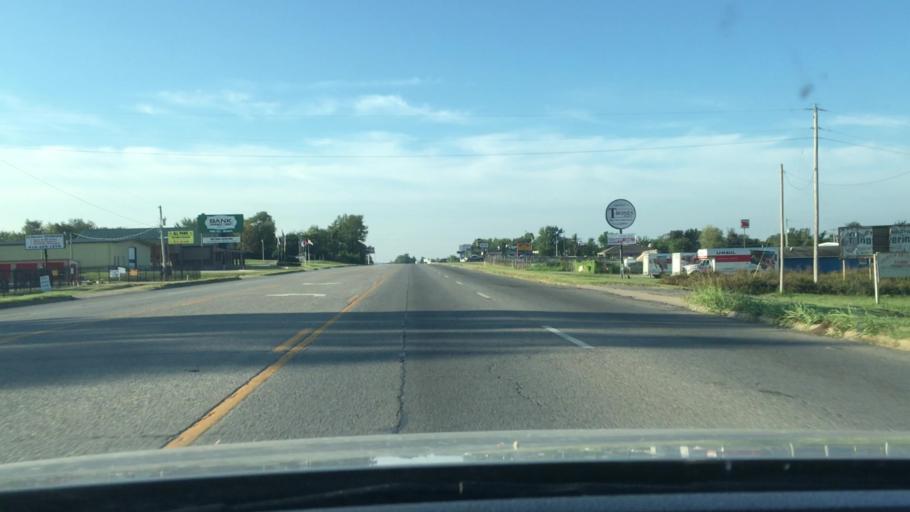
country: US
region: Oklahoma
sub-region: Cherokee County
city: Park Hill
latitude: 35.8695
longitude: -94.9763
